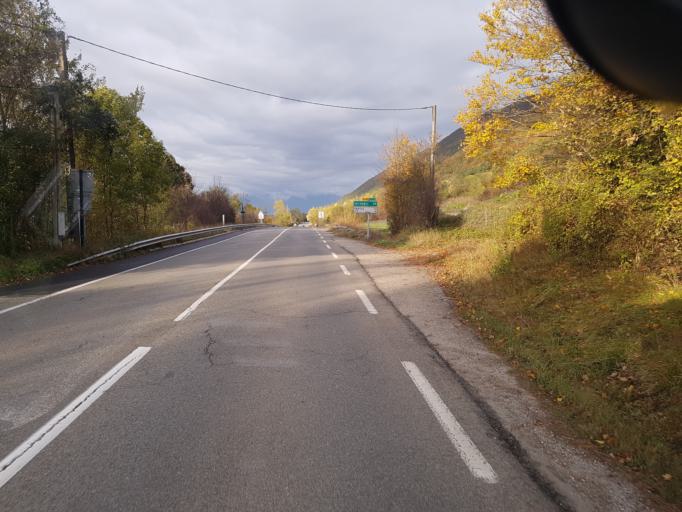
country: FR
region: Rhone-Alpes
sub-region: Departement de l'Isere
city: Le Gua
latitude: 44.9915
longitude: 5.6497
